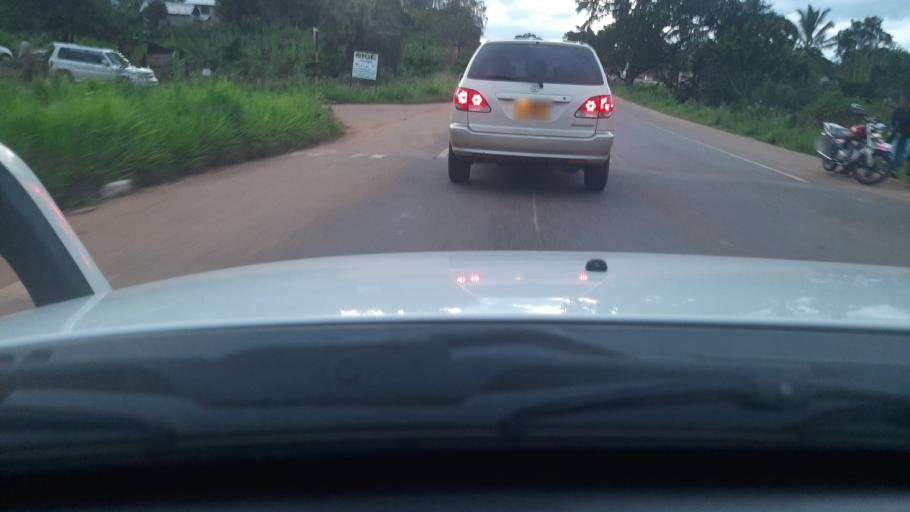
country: TZ
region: Tanga
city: Muheza
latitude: -5.1741
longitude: 38.8026
